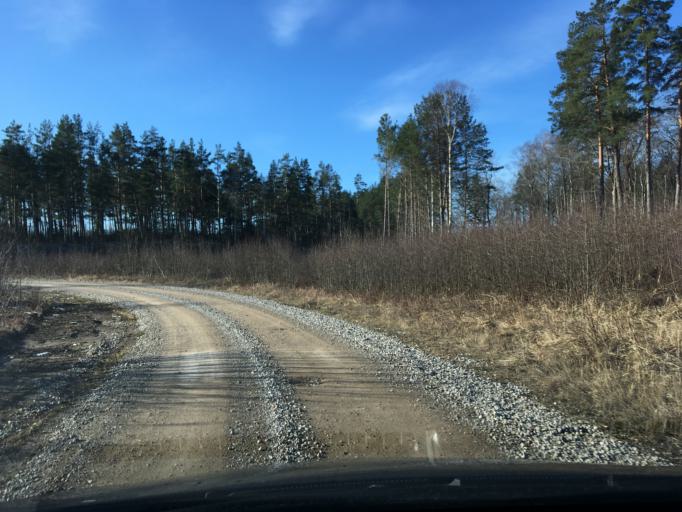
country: EE
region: Laeaene
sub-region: Lihula vald
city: Lihula
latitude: 58.5686
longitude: 23.6913
